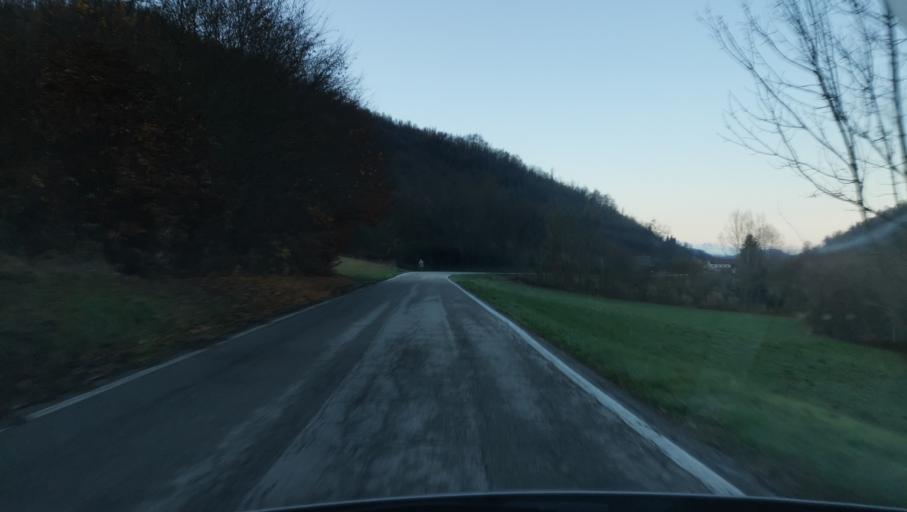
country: IT
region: Piedmont
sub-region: Provincia di Asti
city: Berzano di San Pietro
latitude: 45.1078
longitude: 7.9418
